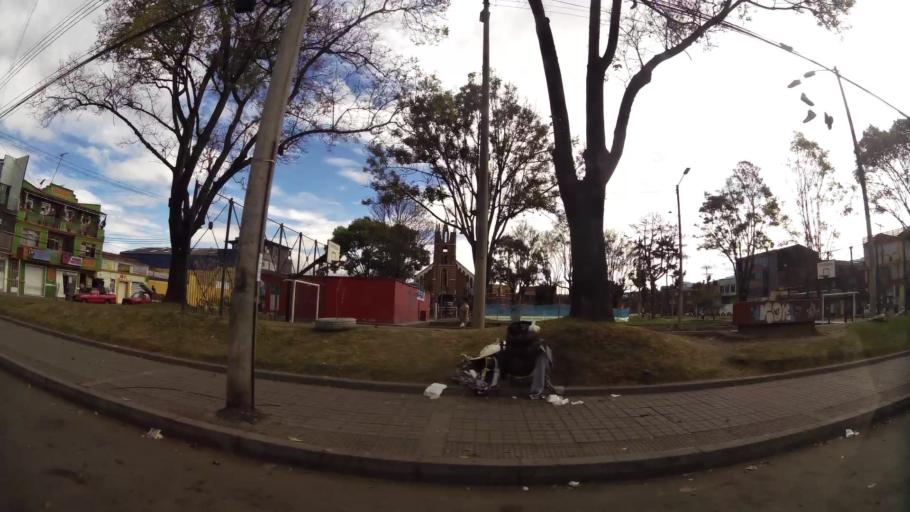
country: CO
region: Bogota D.C.
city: Bogota
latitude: 4.6315
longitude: -74.1088
